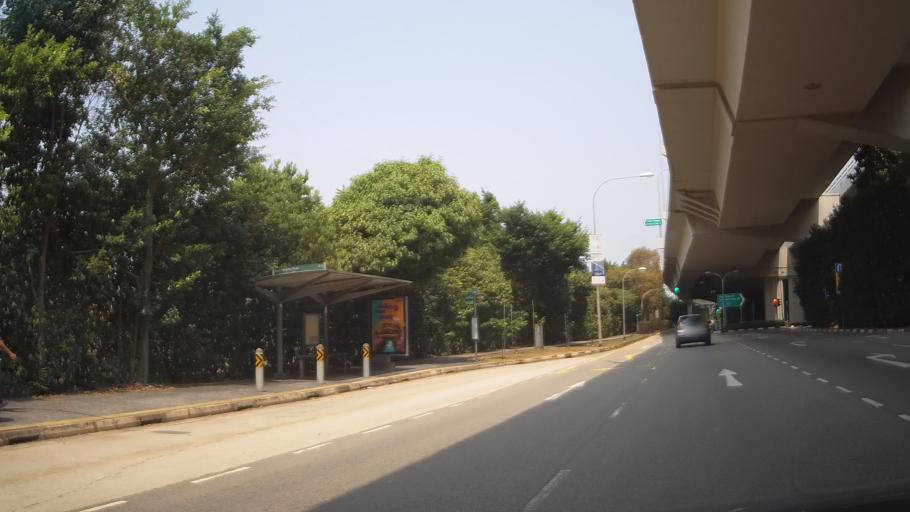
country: SG
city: Singapore
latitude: 1.2780
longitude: 103.7865
